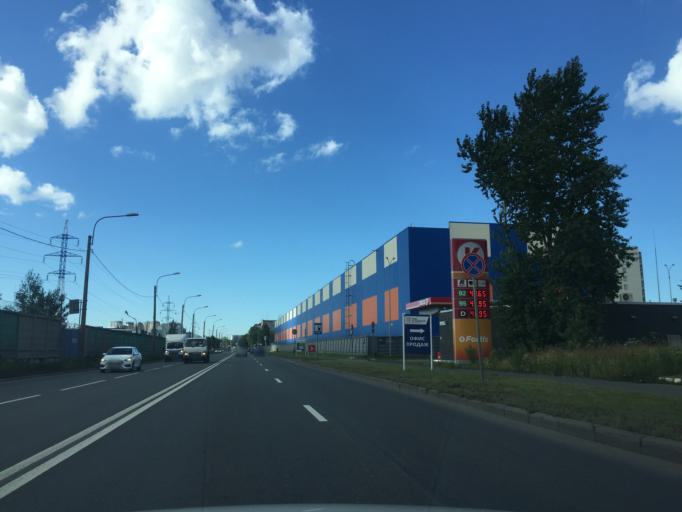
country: RU
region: St.-Petersburg
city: Dachnoye
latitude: 59.8375
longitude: 30.3039
